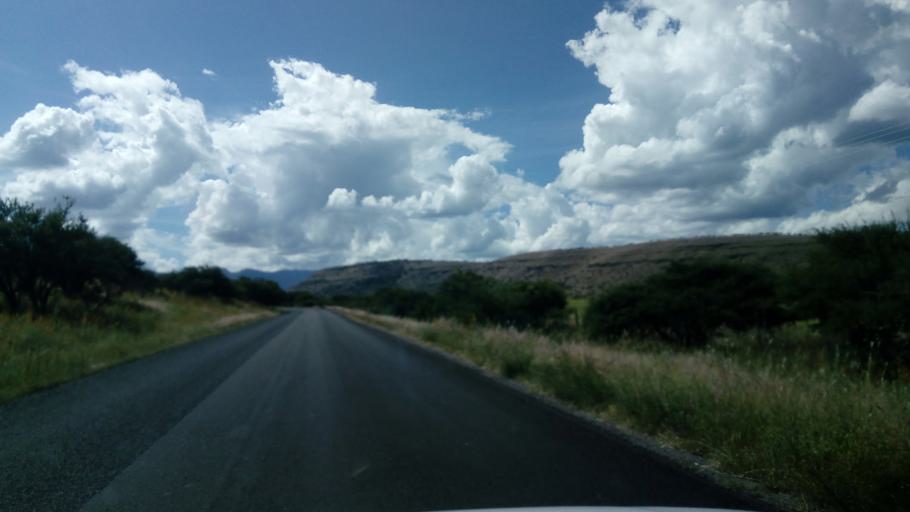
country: MX
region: Durango
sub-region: Durango
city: Jose Refugio Salcido
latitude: 23.8302
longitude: -104.4820
